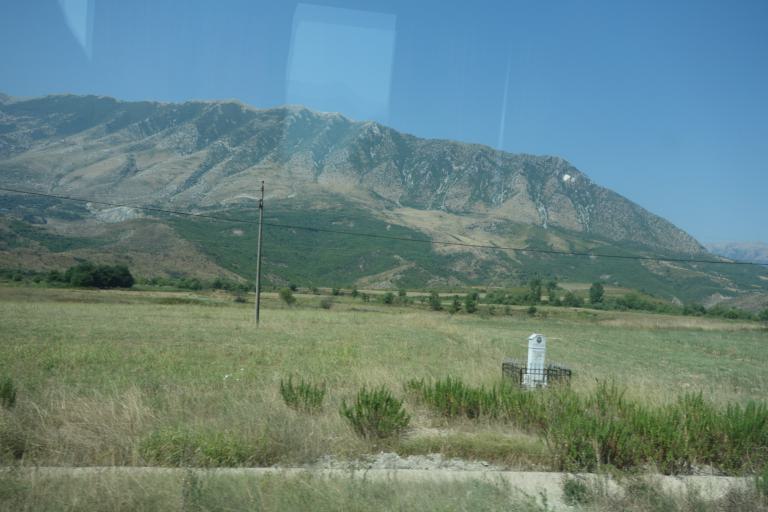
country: AL
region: Gjirokaster
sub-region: Rrethi i Gjirokastres
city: Picar
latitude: 40.1359
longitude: 20.1028
